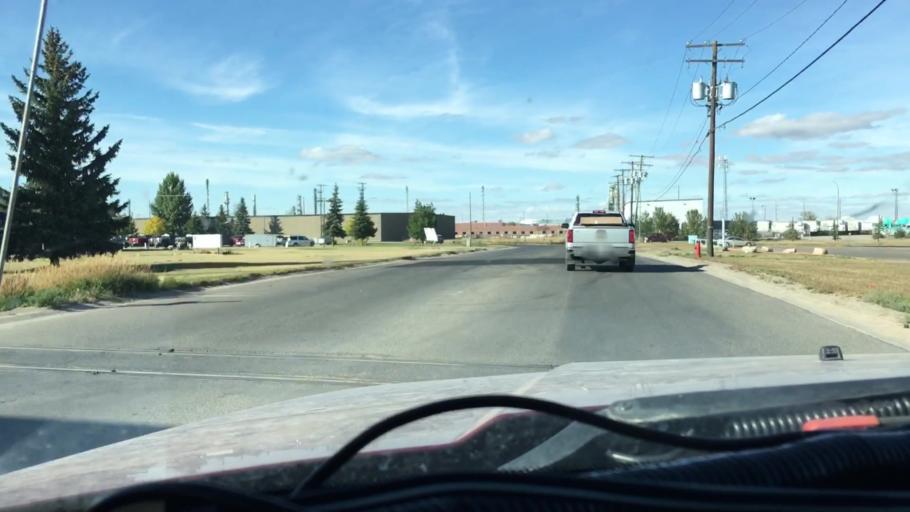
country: CA
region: Saskatchewan
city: Regina
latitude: 50.4766
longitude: -104.5615
